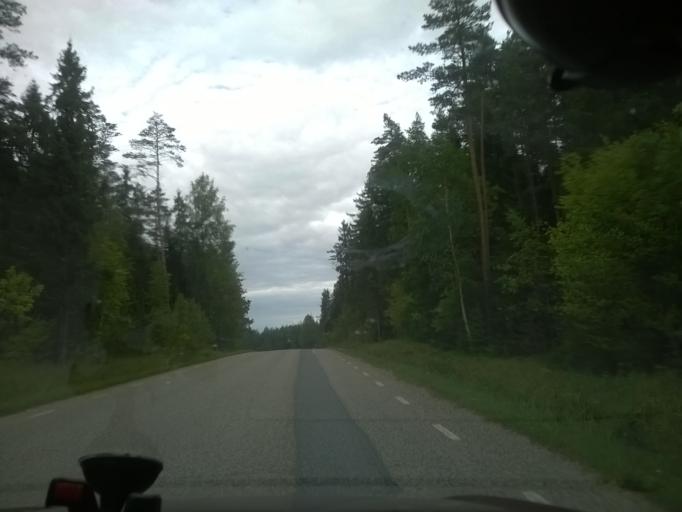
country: EE
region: Vorumaa
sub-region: Voru linn
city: Voru
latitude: 57.7417
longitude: 26.9538
